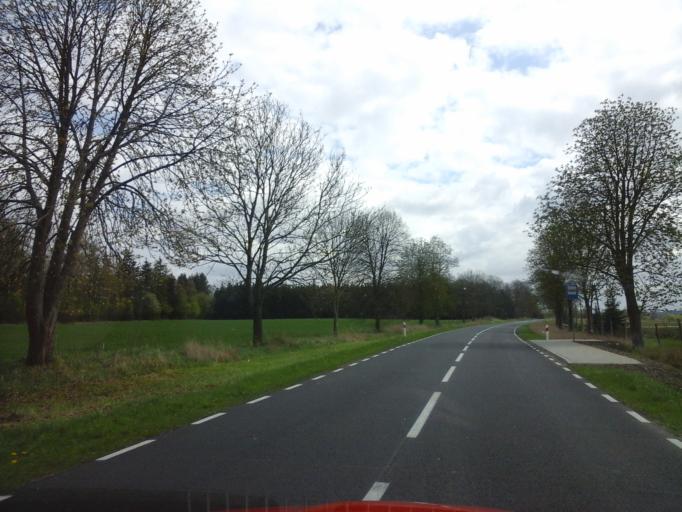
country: PL
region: West Pomeranian Voivodeship
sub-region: Powiat choszczenski
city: Bierzwnik
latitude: 53.0660
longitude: 15.6599
